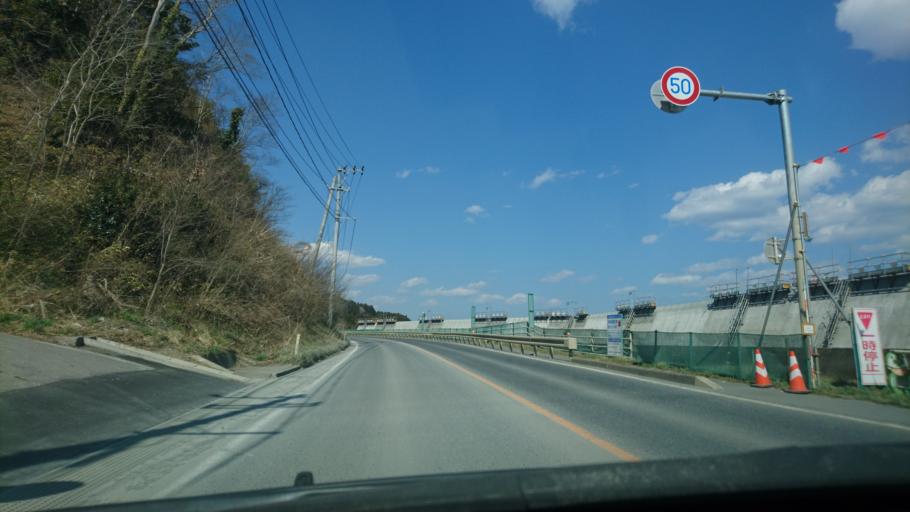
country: JP
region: Miyagi
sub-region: Oshika Gun
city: Onagawa Cho
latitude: 38.6489
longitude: 141.4427
